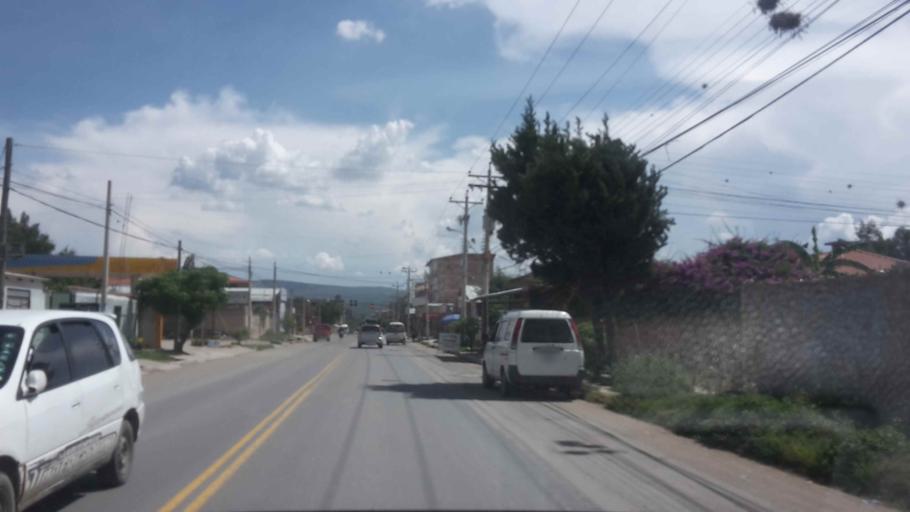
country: BO
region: Cochabamba
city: Cochabamba
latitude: -17.3832
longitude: -66.2362
